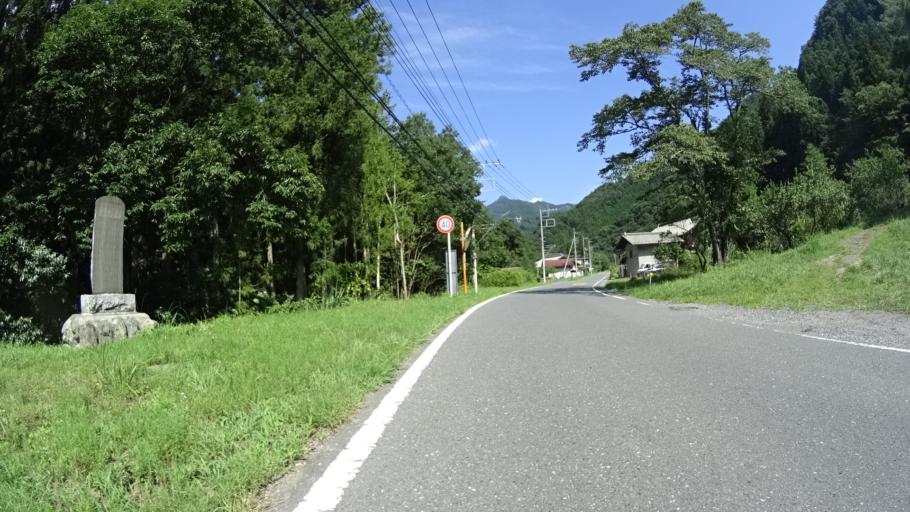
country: JP
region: Saitama
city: Chichibu
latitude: 36.0411
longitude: 138.8946
